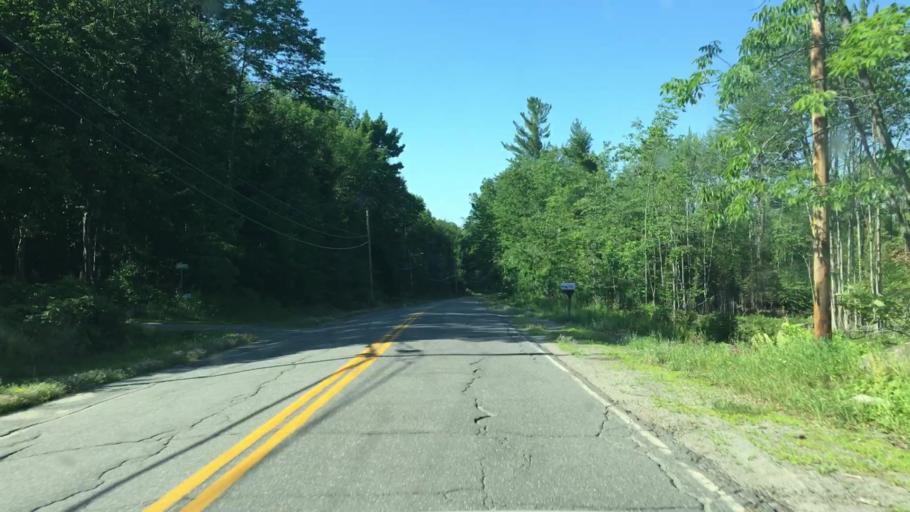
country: US
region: Maine
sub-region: Penobscot County
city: Enfield
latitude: 45.2675
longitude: -68.5619
